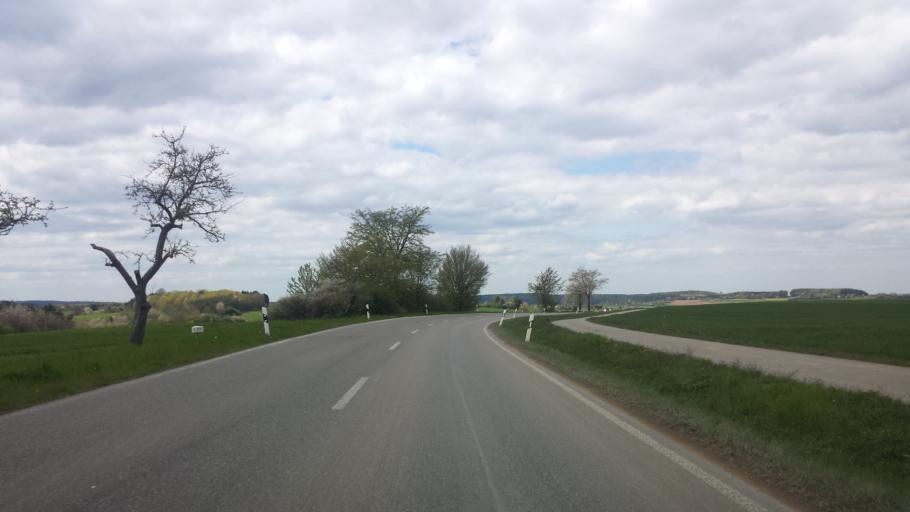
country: DE
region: Baden-Wuerttemberg
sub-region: Karlsruhe Region
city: Monsheim
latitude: 48.8552
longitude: 8.8958
